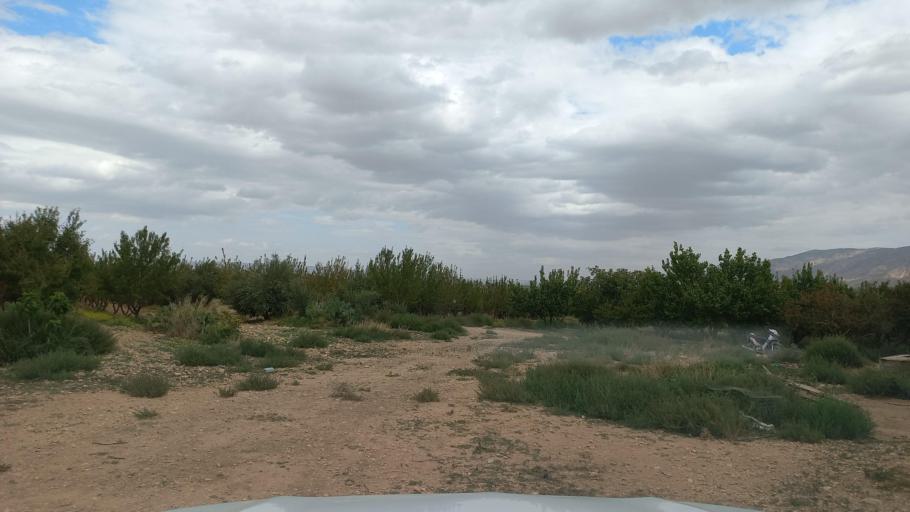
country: TN
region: Al Qasrayn
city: Sbiba
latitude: 35.3799
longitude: 9.1288
